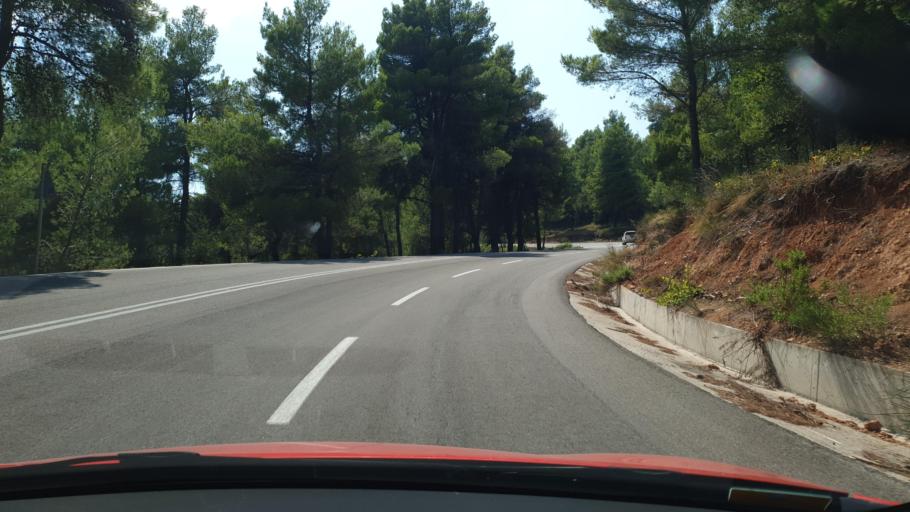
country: GR
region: Central Greece
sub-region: Nomos Evvoias
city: Politika
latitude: 38.6356
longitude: 23.5706
